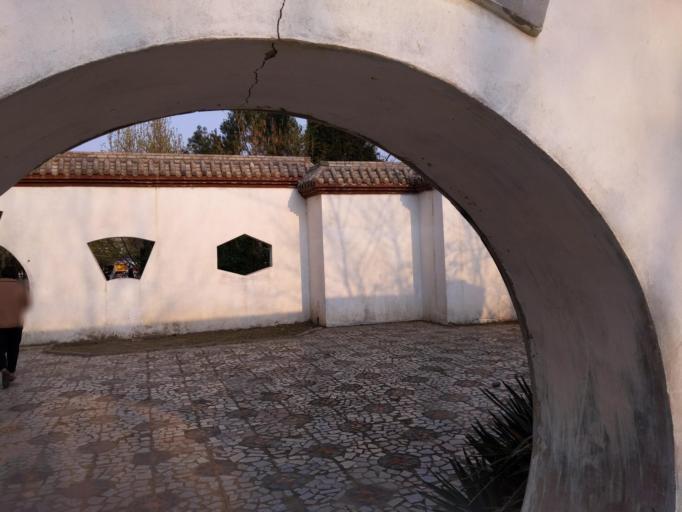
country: CN
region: Henan Sheng
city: Puyang
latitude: 35.7519
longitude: 115.0274
